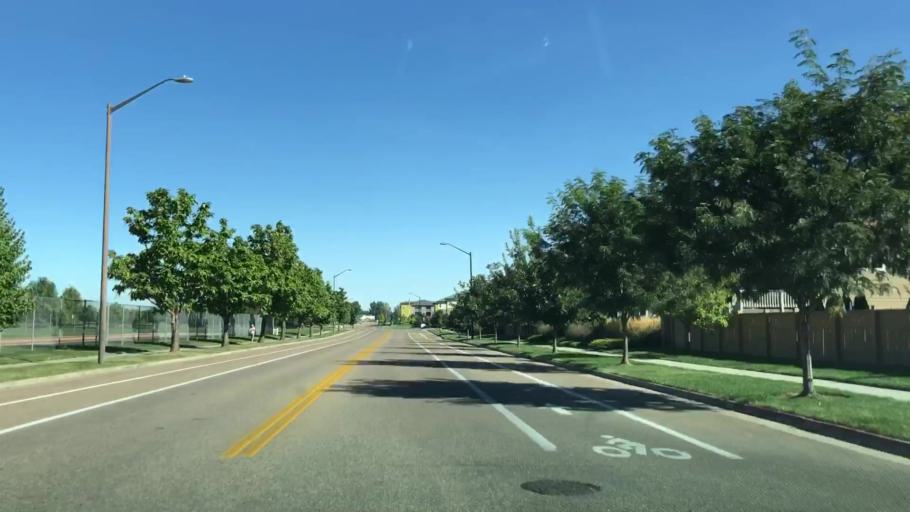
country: US
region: Colorado
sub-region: Larimer County
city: Fort Collins
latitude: 40.5145
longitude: -105.0106
